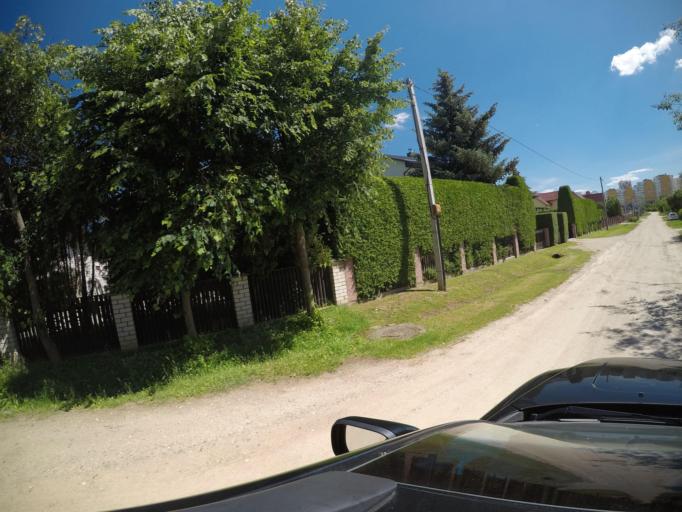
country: BY
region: Grodnenskaya
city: Hrodna
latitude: 53.7197
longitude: 23.8566
